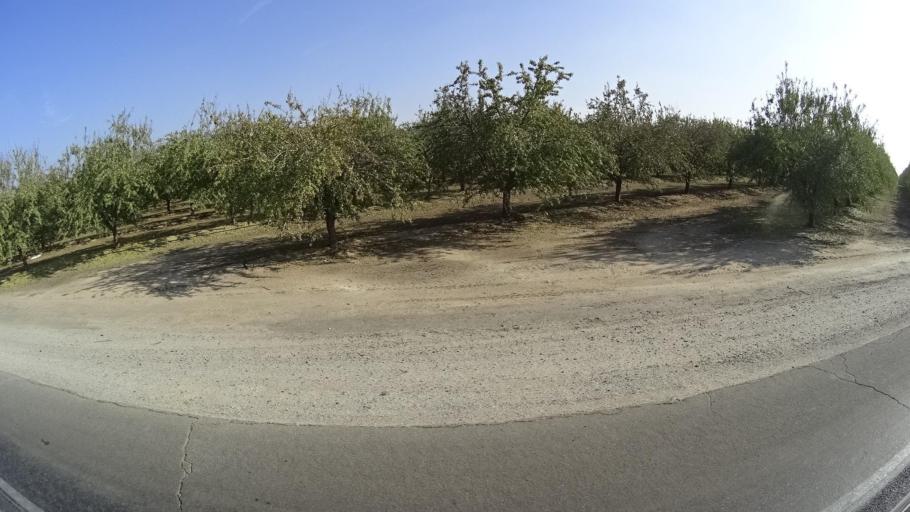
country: US
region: California
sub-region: Kern County
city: McFarland
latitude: 35.6976
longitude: -119.1722
